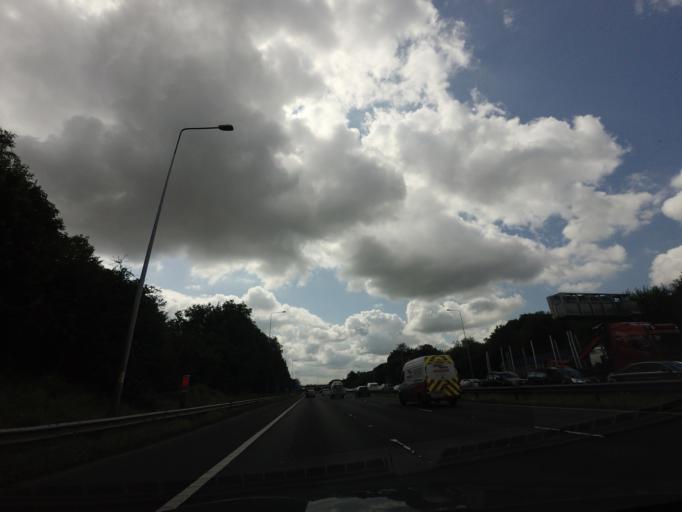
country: GB
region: England
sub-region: Borough of Wigan
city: Shevington
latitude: 53.5969
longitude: -2.6927
